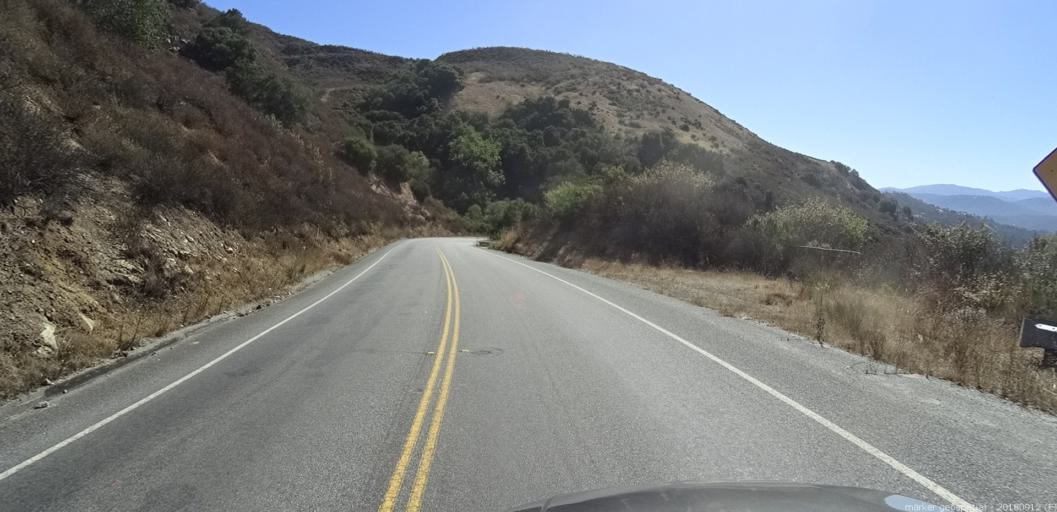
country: US
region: California
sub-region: Monterey County
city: Carmel Valley Village
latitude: 36.5156
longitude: -121.7578
